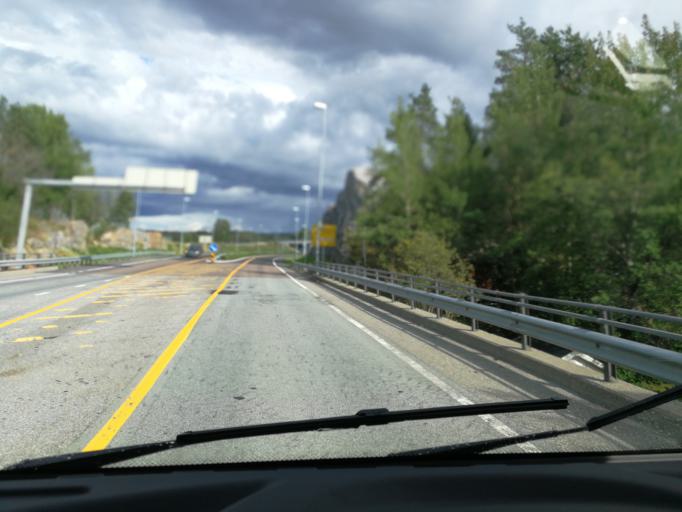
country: NO
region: Ostfold
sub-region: Marker
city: Orje
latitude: 59.4828
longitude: 11.6537
